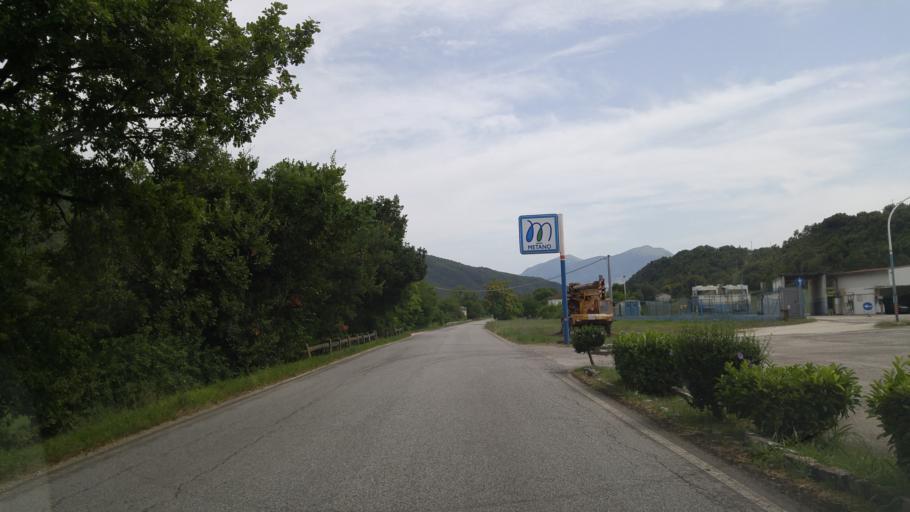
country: IT
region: The Marches
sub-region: Provincia di Pesaro e Urbino
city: Acqualagna
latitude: 43.6093
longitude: 12.6738
